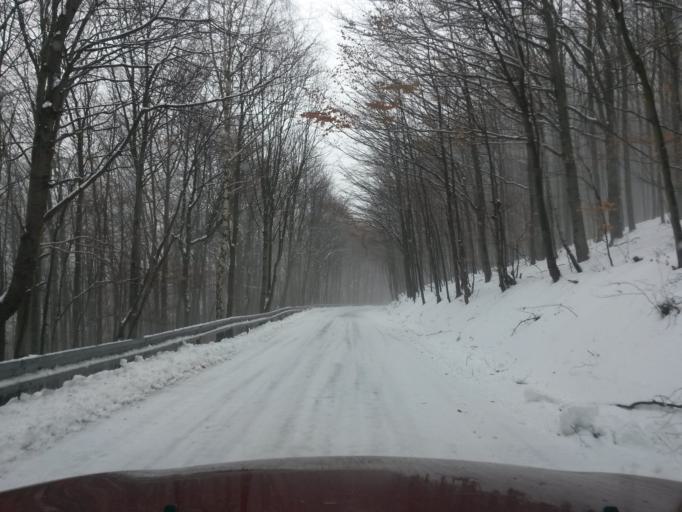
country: SK
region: Kosicky
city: Secovce
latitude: 48.8122
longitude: 21.5322
